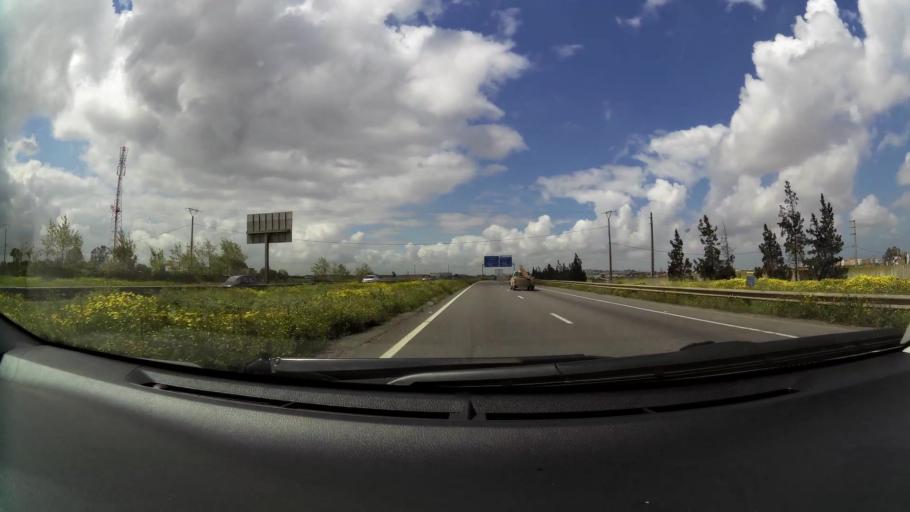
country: MA
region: Grand Casablanca
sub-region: Mediouna
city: Tit Mellil
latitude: 33.5323
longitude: -7.5558
